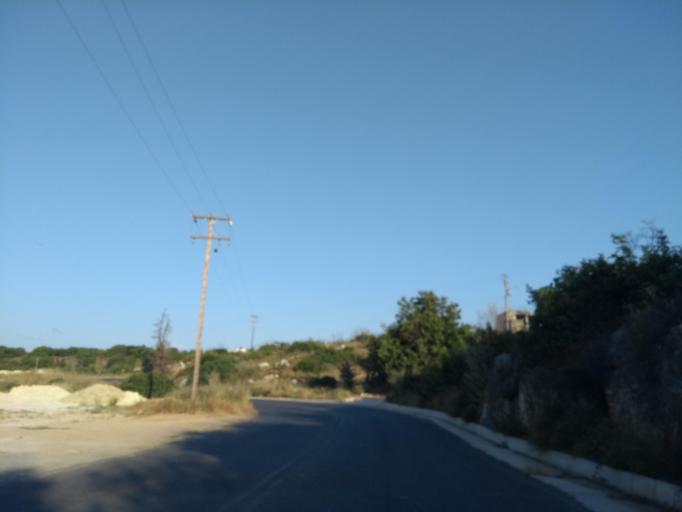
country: GR
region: Crete
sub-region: Nomos Chanias
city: Kalivai
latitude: 35.4285
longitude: 24.1794
